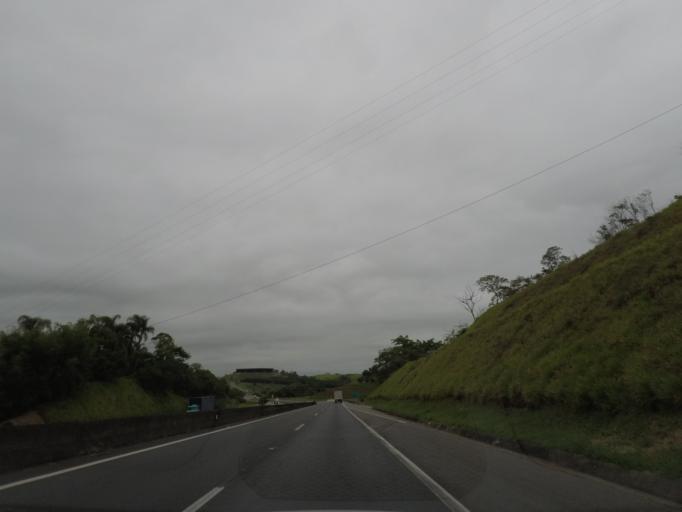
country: BR
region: Sao Paulo
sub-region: Jacarei
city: Jacarei
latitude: -23.2615
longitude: -46.0668
